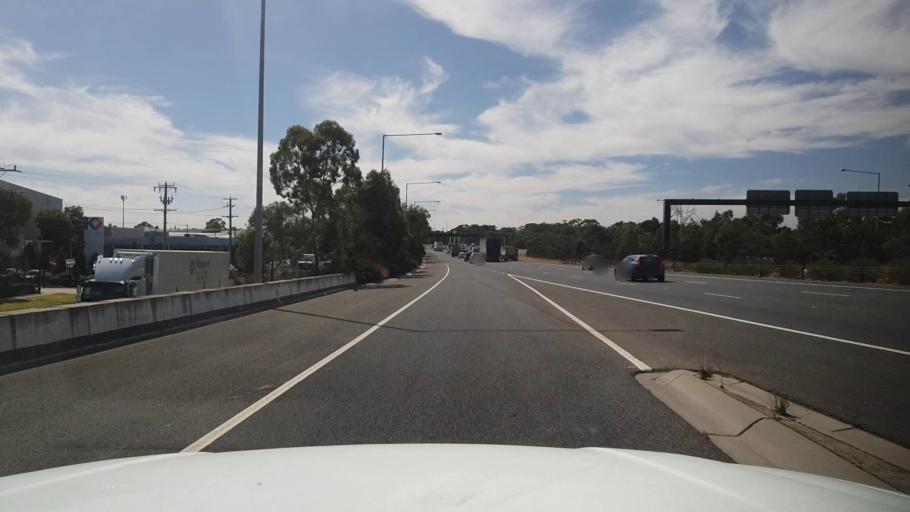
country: AU
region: Victoria
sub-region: Greater Dandenong
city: Dandenong
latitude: -37.9889
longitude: 145.1923
